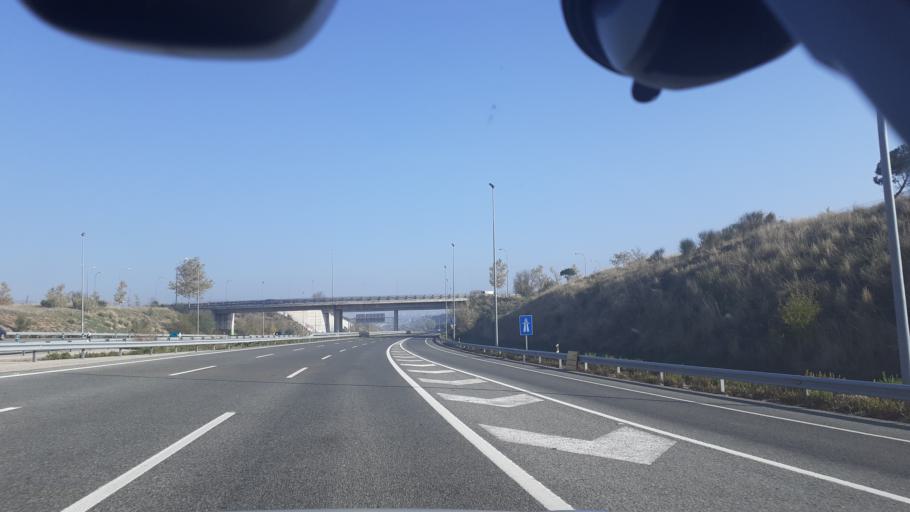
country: ES
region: Madrid
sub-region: Provincia de Madrid
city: Vicalvaro
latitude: 40.4135
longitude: -3.6129
